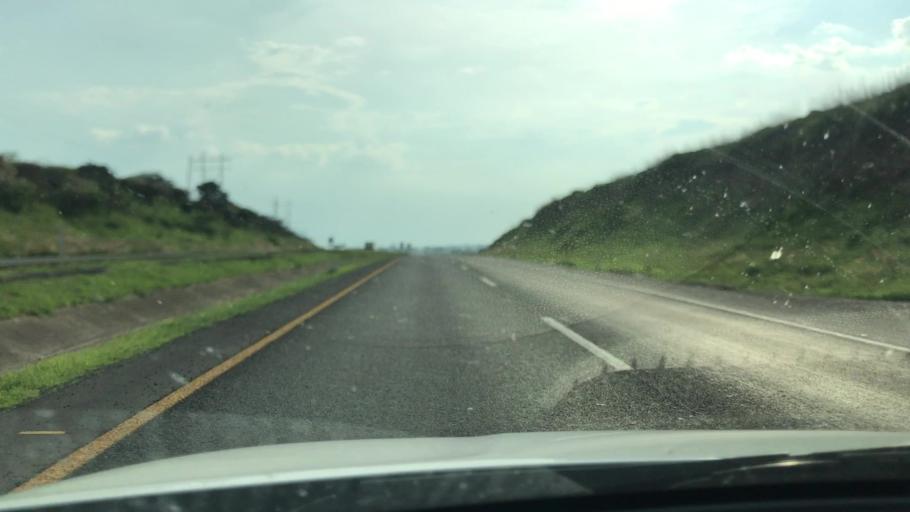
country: MX
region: Guanajuato
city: Penjamo
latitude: 20.3842
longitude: -101.7924
